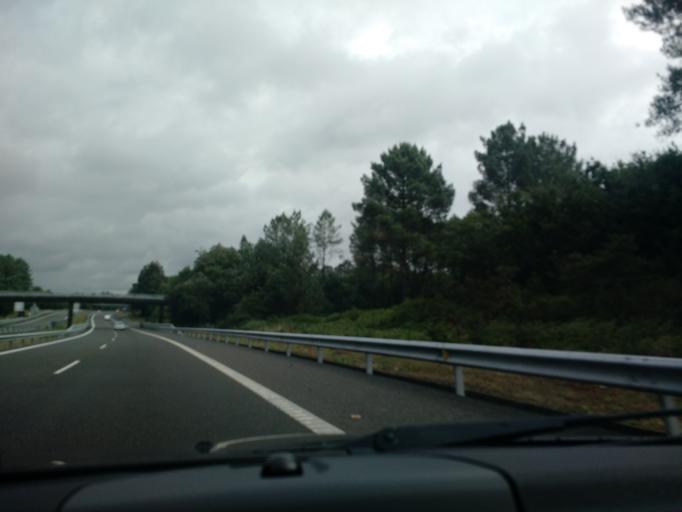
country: ES
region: Galicia
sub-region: Provincia da Coruna
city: Oroso
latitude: 42.9844
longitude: -8.4333
